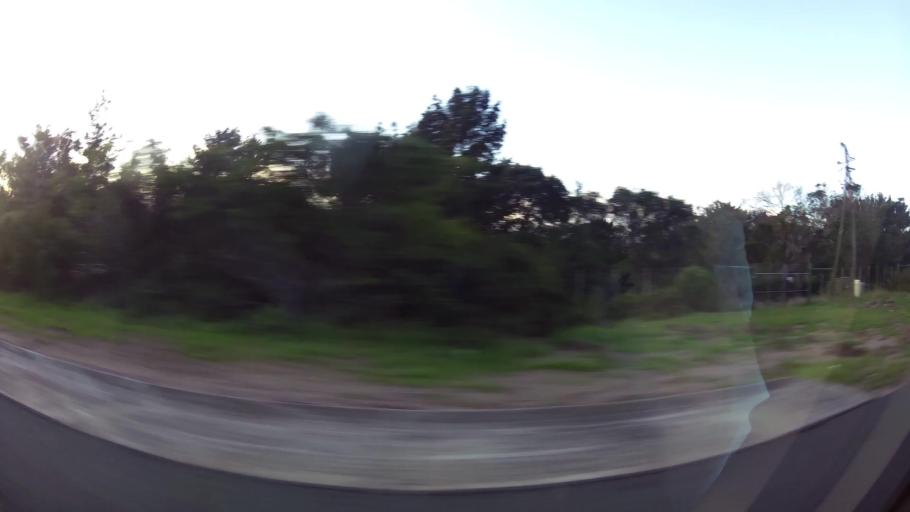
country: ZA
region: Western Cape
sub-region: Eden District Municipality
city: George
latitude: -34.0041
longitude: 22.7175
